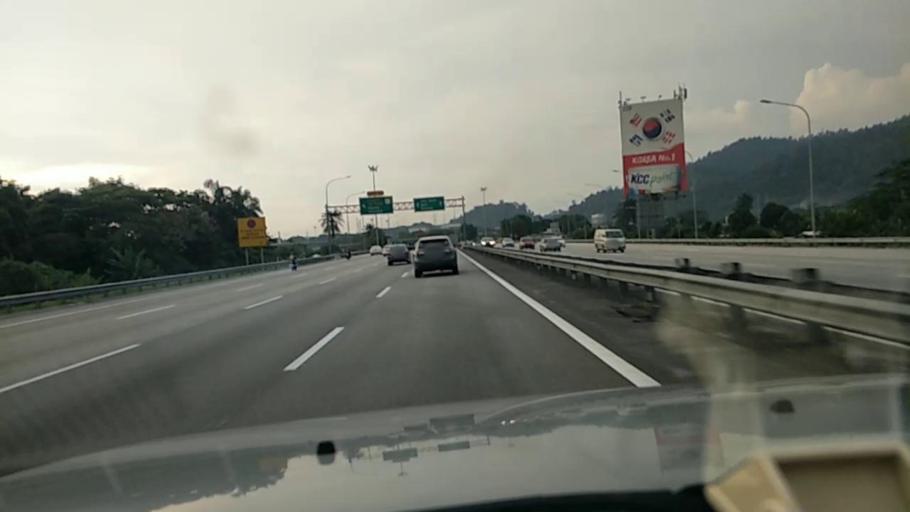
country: MY
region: Selangor
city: Kuang
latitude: 3.2192
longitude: 101.5790
